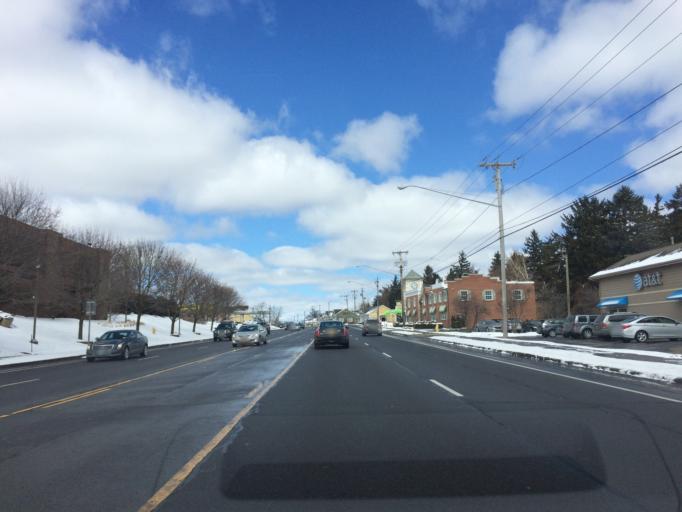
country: US
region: New York
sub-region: Monroe County
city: Pittsford
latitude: 43.1069
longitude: -77.5424
